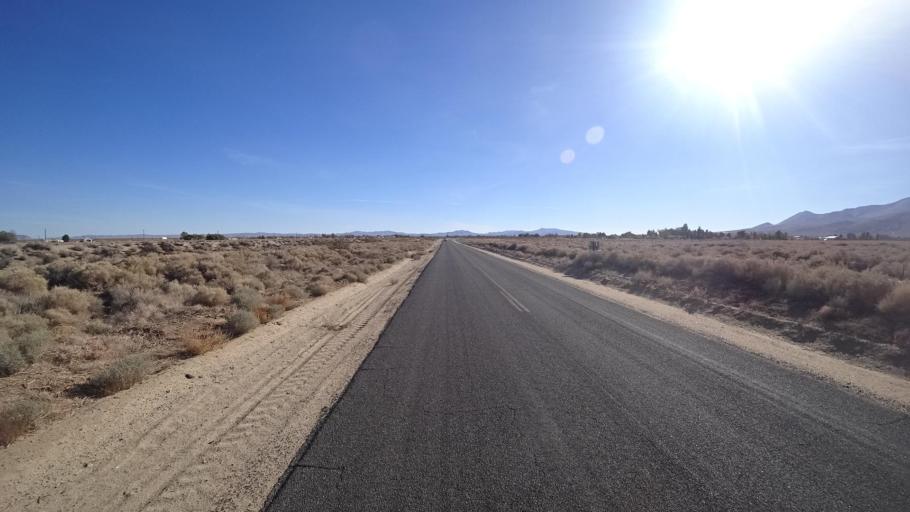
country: US
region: California
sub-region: Kern County
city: Inyokern
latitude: 35.7204
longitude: -117.8353
